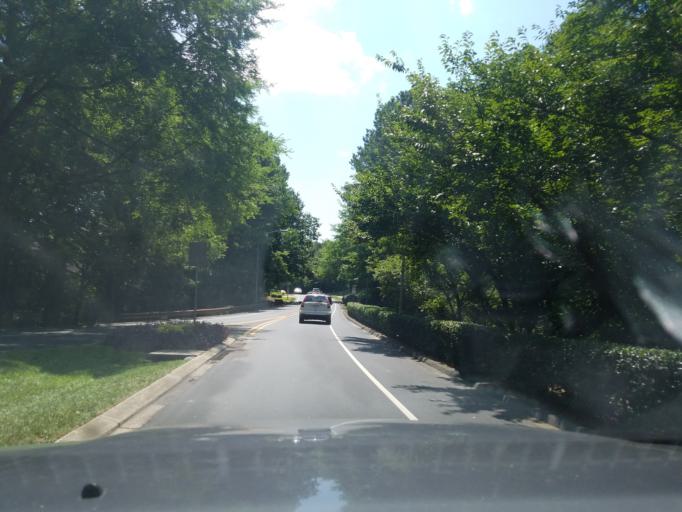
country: US
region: North Carolina
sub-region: Durham County
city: Durham
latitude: 35.9236
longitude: -78.9415
